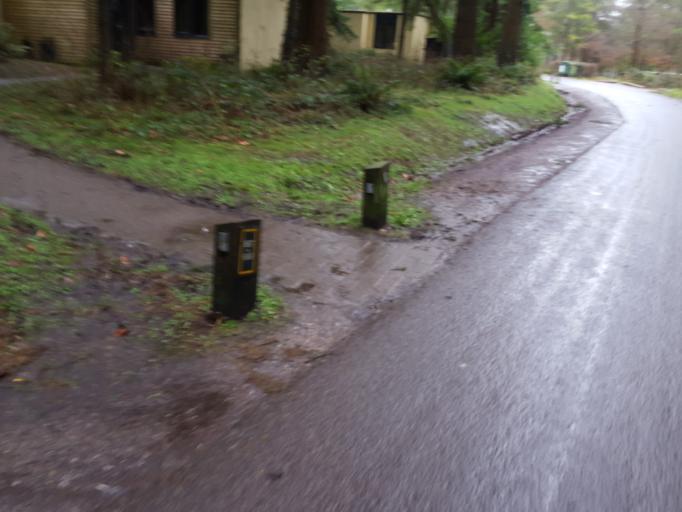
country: GB
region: England
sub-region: Wiltshire
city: Corsley
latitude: 51.1771
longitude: -2.2380
